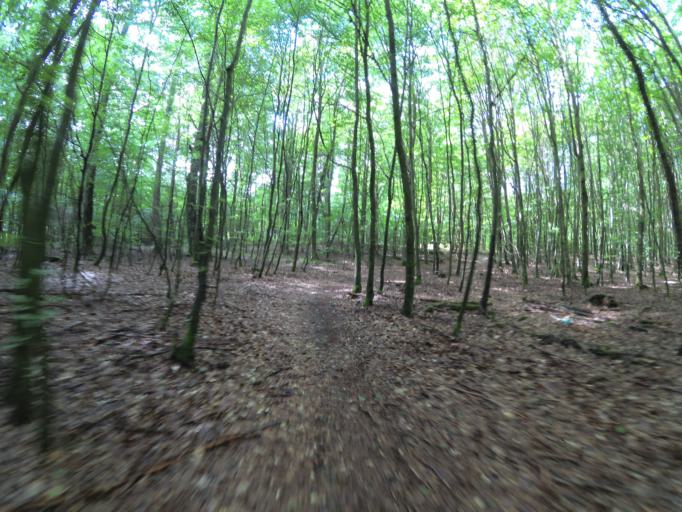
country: PL
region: Pomeranian Voivodeship
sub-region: Gdynia
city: Wielki Kack
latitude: 54.5078
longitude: 18.4497
